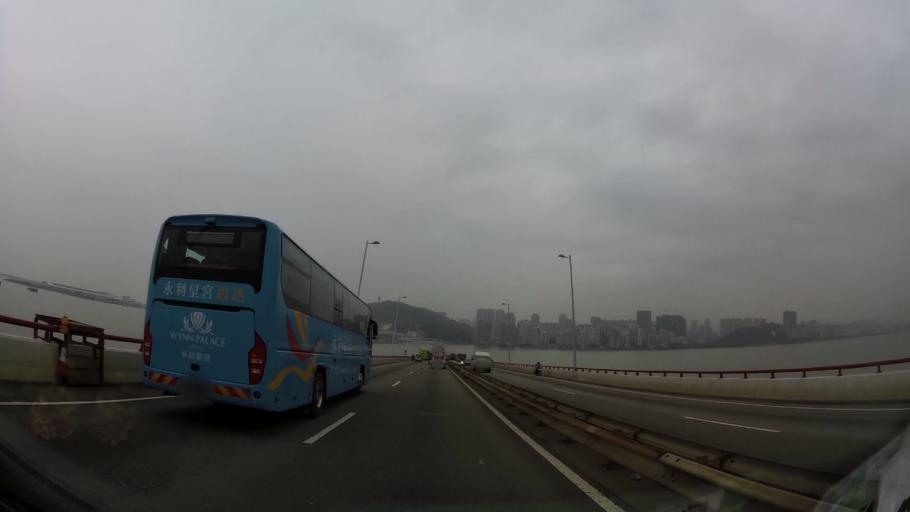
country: MO
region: Macau
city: Macau
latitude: 22.1777
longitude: 113.5635
